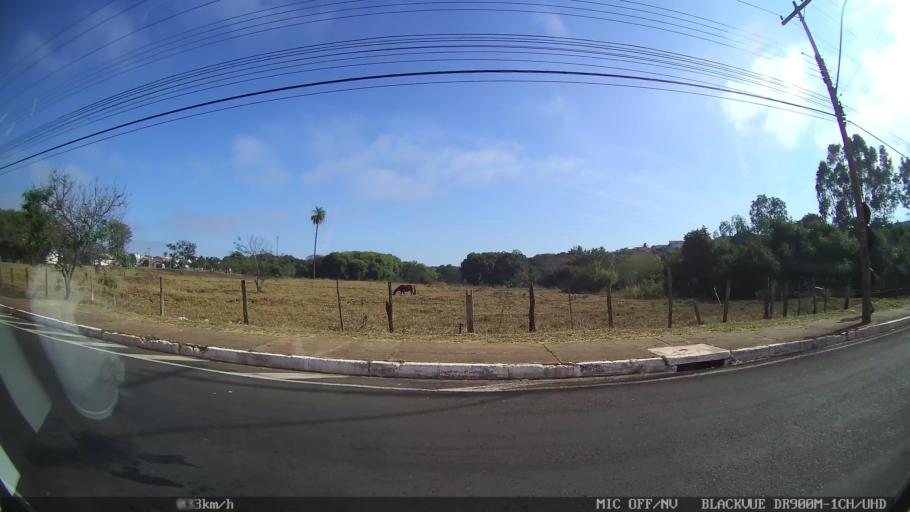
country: BR
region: Sao Paulo
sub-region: Sao Jose Do Rio Preto
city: Sao Jose do Rio Preto
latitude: -20.7962
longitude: -49.4271
